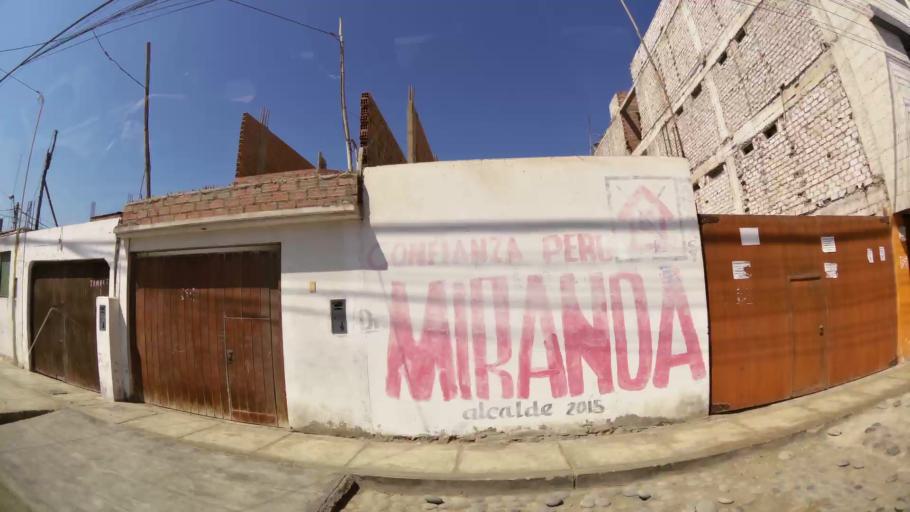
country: PE
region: Lima
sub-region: Provincia de Canete
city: San Vicente de Canete
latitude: -13.0267
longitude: -76.4798
